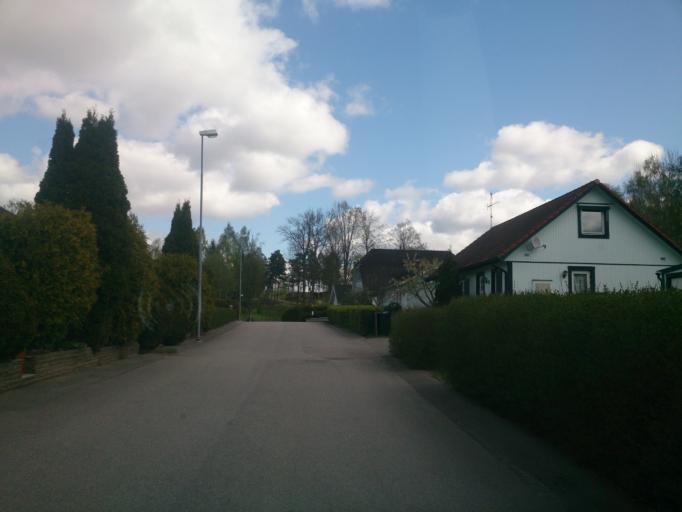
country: SE
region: OEstergoetland
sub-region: Atvidabergs Kommun
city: Atvidaberg
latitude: 58.2024
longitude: 15.9802
